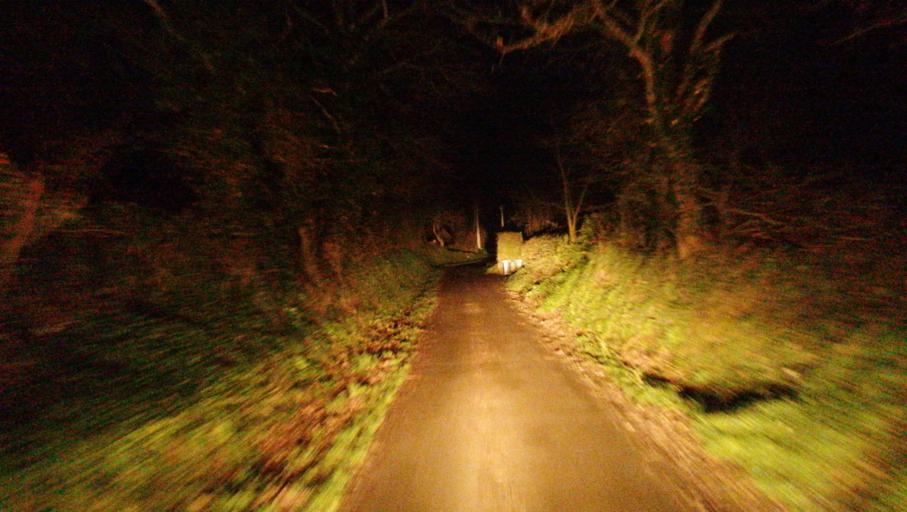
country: FR
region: Brittany
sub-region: Departement des Cotes-d'Armor
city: Plehedel
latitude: 48.6793
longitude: -3.0313
